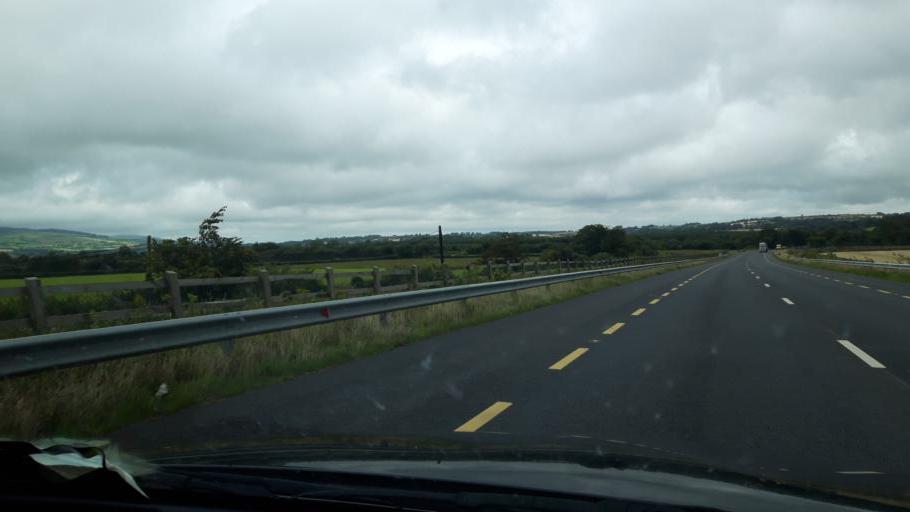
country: IE
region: Leinster
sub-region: Loch Garman
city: New Ross
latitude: 52.4223
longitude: -6.8516
